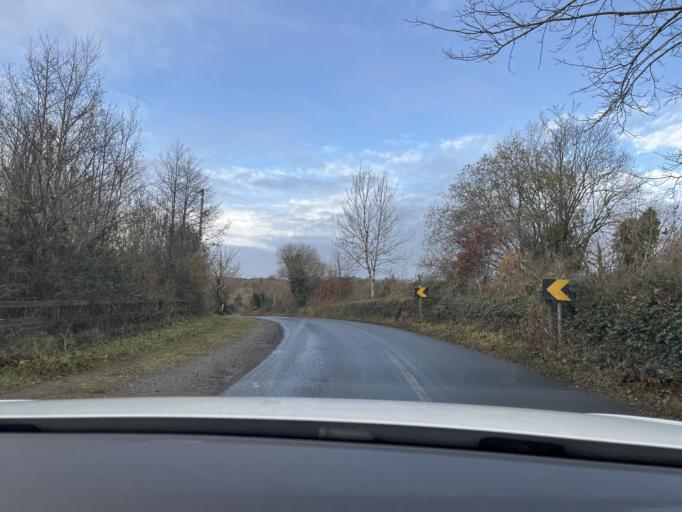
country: IE
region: Connaught
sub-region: Sligo
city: Sligo
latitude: 54.2646
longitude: -8.3628
